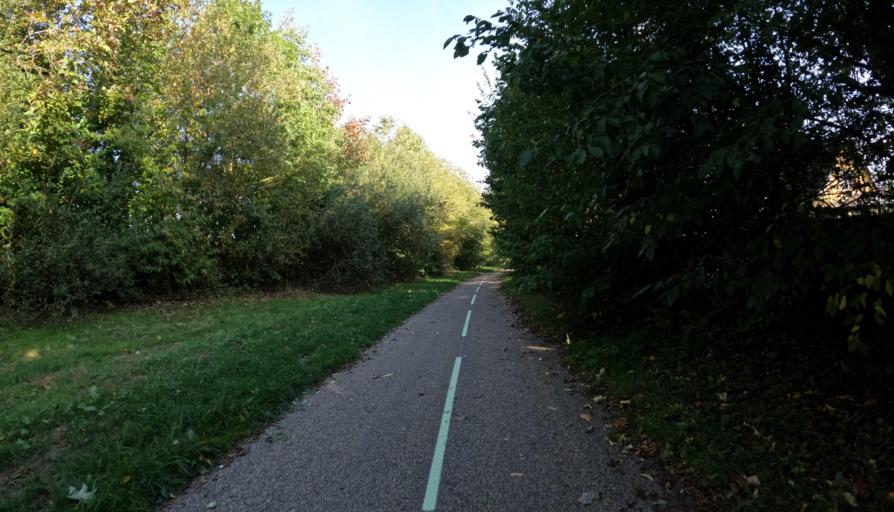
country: FR
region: Brittany
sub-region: Departement d'Ille-et-Vilaine
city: Betton
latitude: 48.1590
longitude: -1.6350
